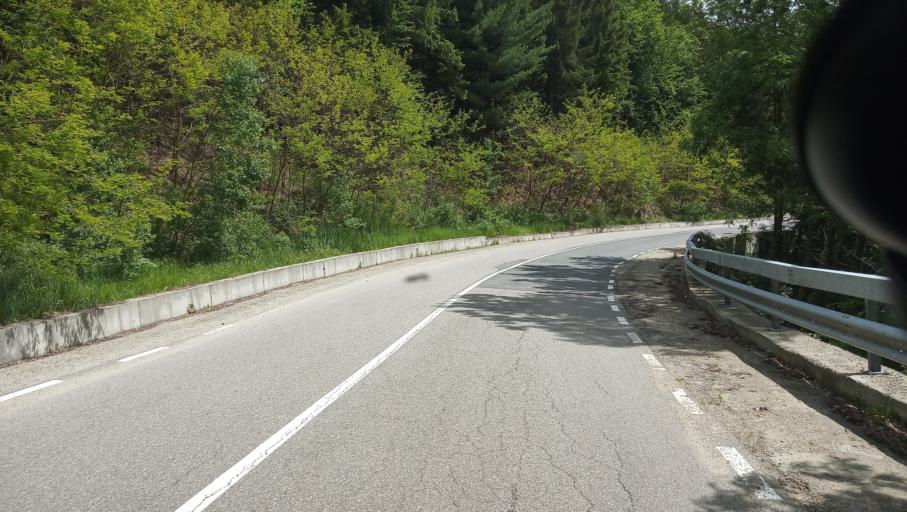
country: RO
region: Caras-Severin
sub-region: Comuna Brebu Nou
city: Brebu Nou
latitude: 45.2511
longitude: 22.1585
